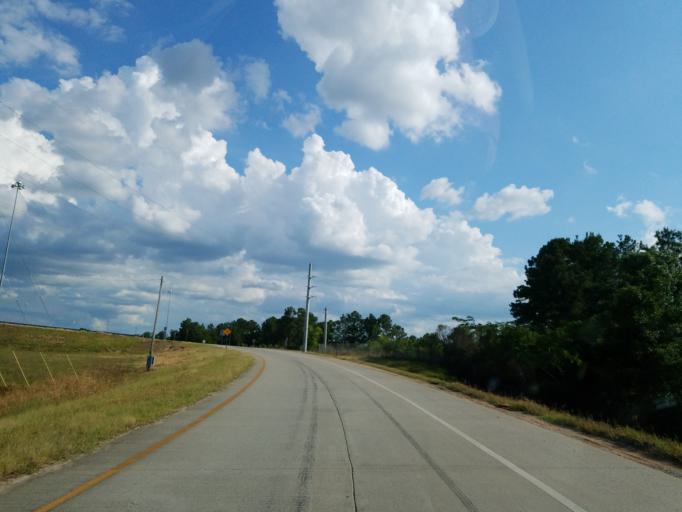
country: US
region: Georgia
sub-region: Crisp County
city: Cordele
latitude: 32.0057
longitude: -83.7601
